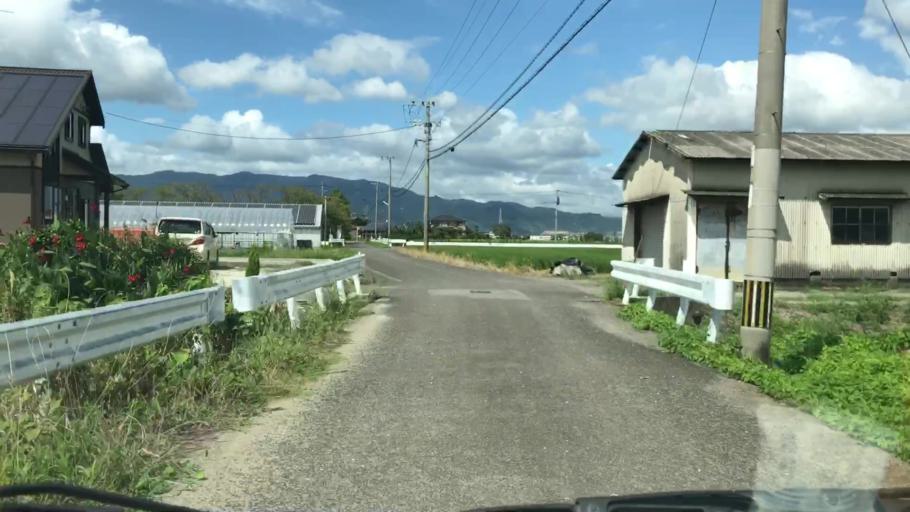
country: JP
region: Saga Prefecture
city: Saga-shi
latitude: 33.2370
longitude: 130.2120
